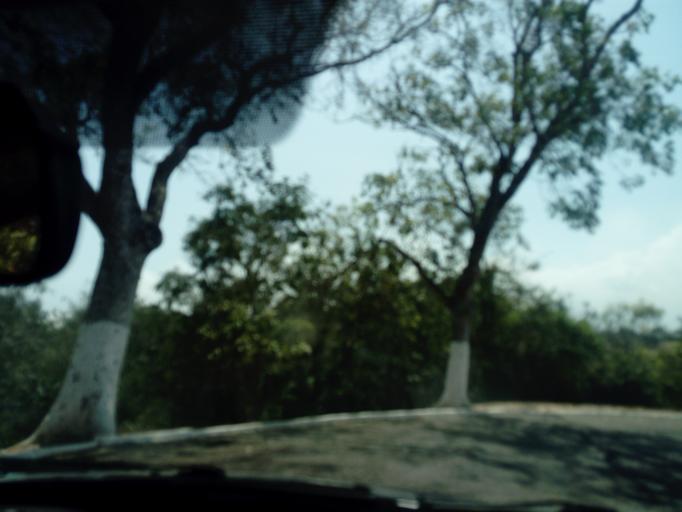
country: GH
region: Central
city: Cape Coast
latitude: 5.1133
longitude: -1.2861
